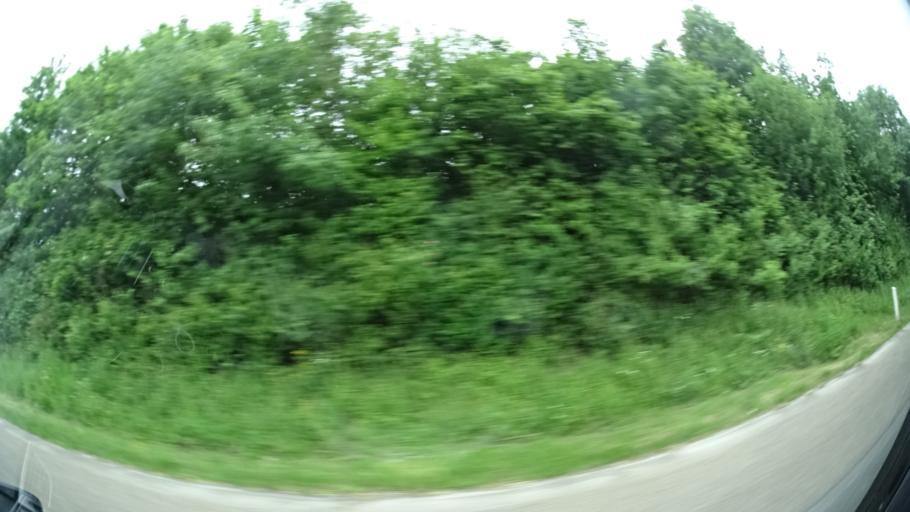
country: DK
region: Central Jutland
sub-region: Arhus Kommune
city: Logten
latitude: 56.2691
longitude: 10.3298
